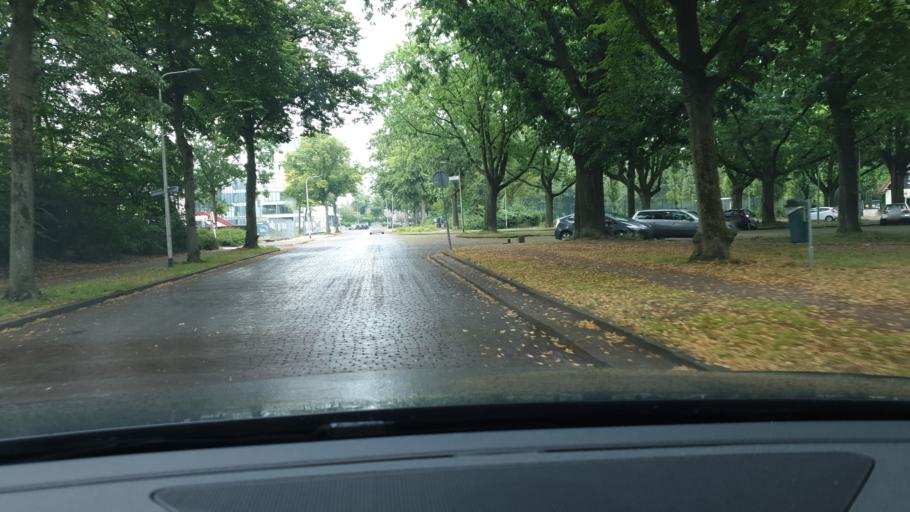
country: NL
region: Gelderland
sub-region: Gemeente Nijmegen
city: Nijmegen
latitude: 51.8284
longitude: 5.8382
